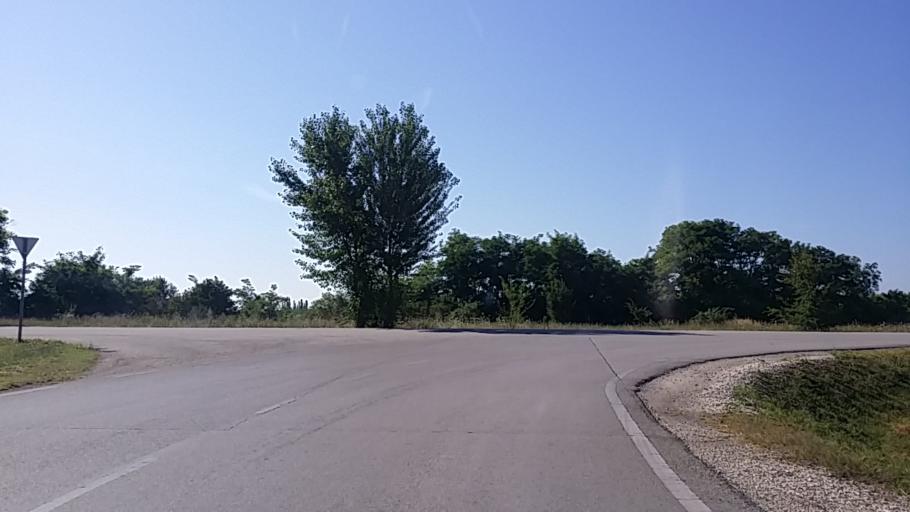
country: HU
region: Fejer
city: Ivancsa
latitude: 47.1320
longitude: 18.8234
